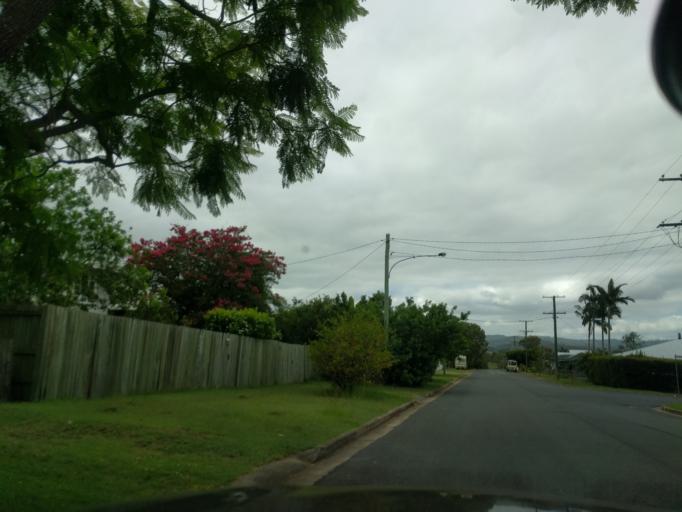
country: AU
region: Queensland
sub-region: Logan
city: Cedar Vale
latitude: -27.9893
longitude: 153.0067
